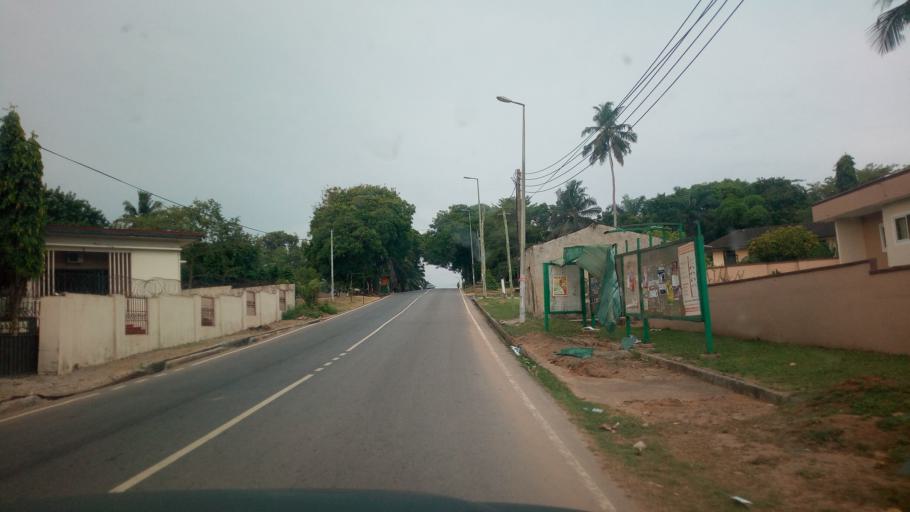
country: GH
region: Western
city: Takoradi
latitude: 4.8805
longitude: -1.7592
